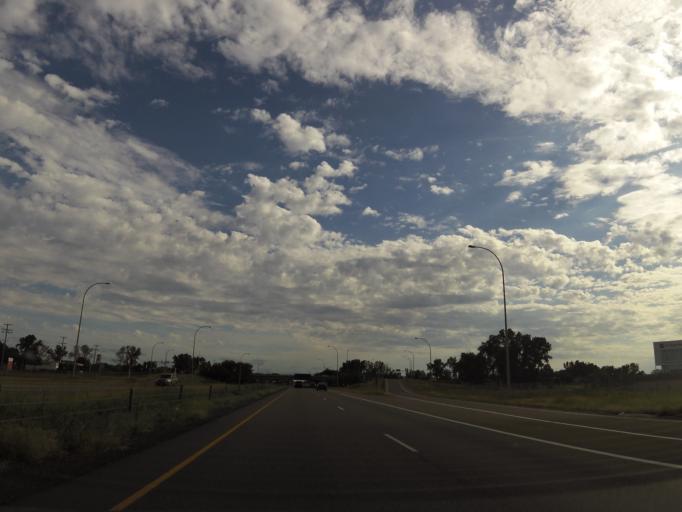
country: US
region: Minnesota
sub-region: Hennepin County
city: New Hope
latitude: 45.0467
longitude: -93.4010
